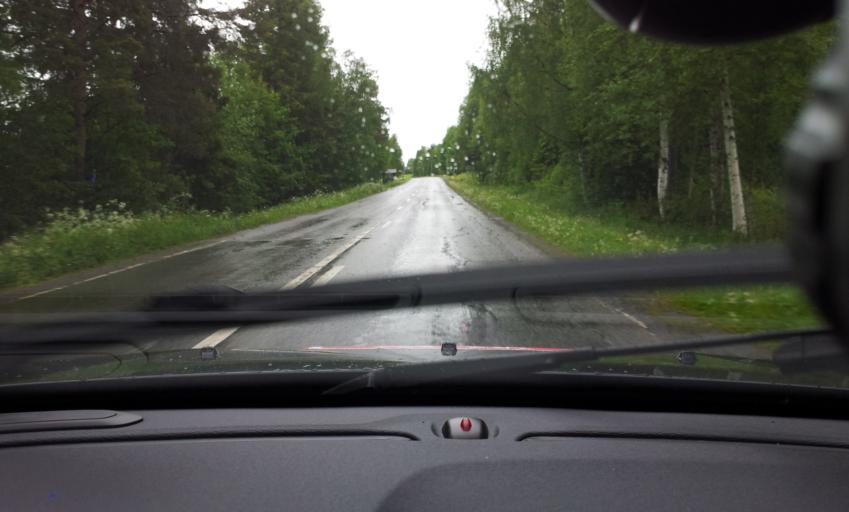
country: SE
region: Jaemtland
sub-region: Krokoms Kommun
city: Krokom
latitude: 63.2972
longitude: 14.4833
